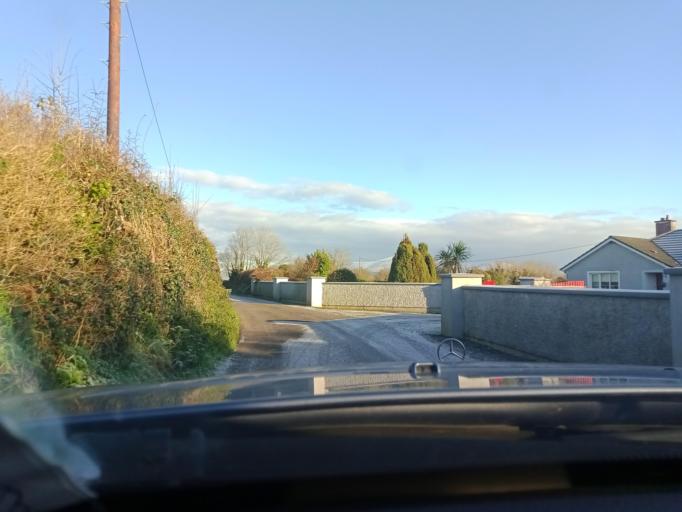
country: IE
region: Leinster
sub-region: Kilkenny
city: Graiguenamanagh
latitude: 52.5569
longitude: -6.9448
